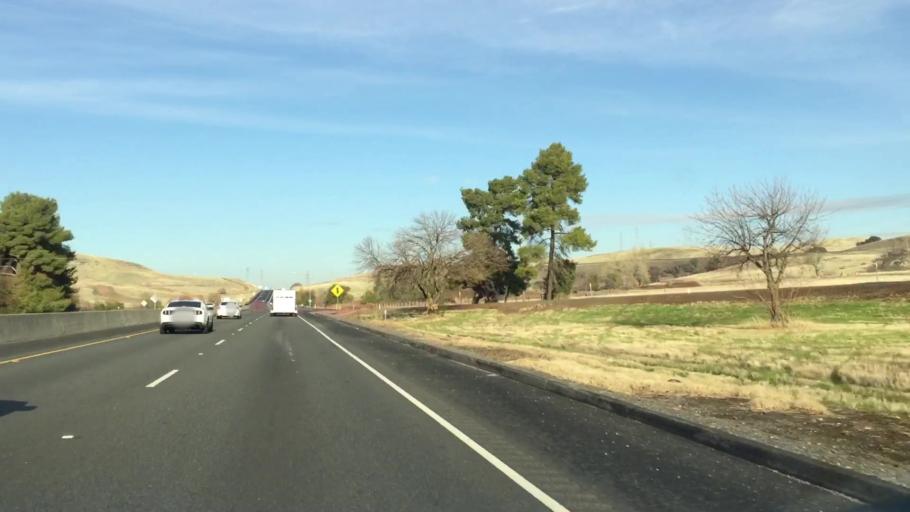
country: US
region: California
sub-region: Butte County
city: Thermalito
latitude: 39.5352
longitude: -121.5829
